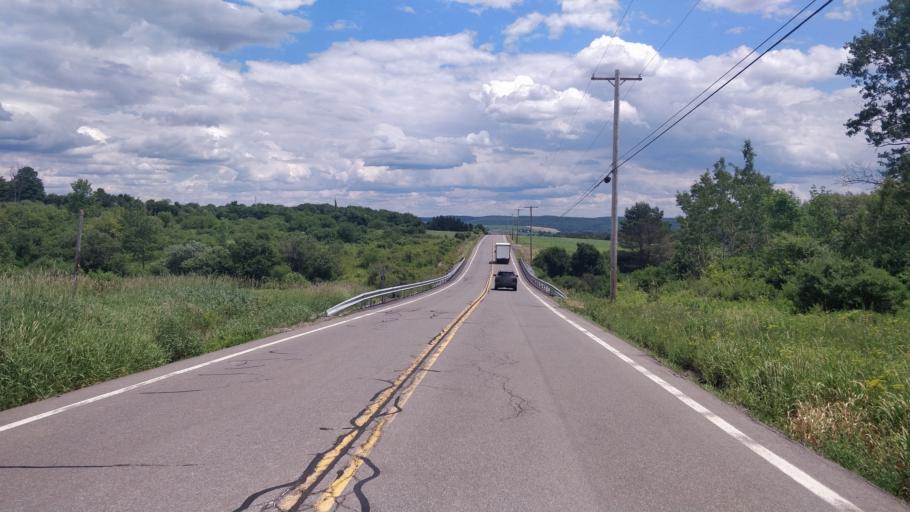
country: US
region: New York
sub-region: Cortland County
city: Homer
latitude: 42.6396
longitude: -76.2204
